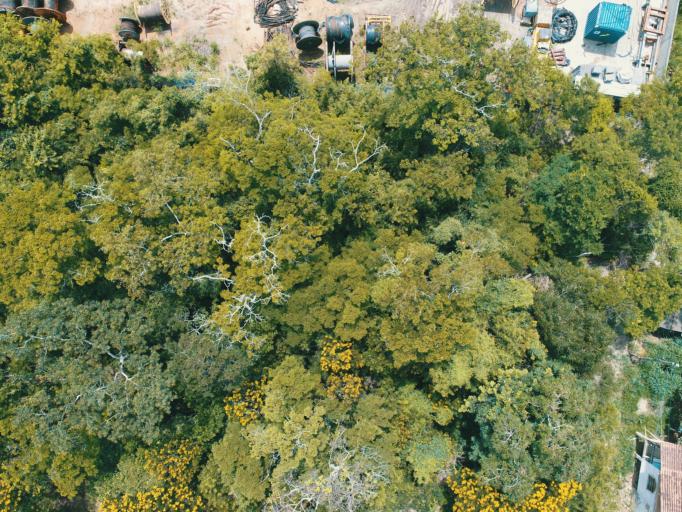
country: BR
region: Rio de Janeiro
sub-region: Macae
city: Macae
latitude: -22.4391
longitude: -41.8695
